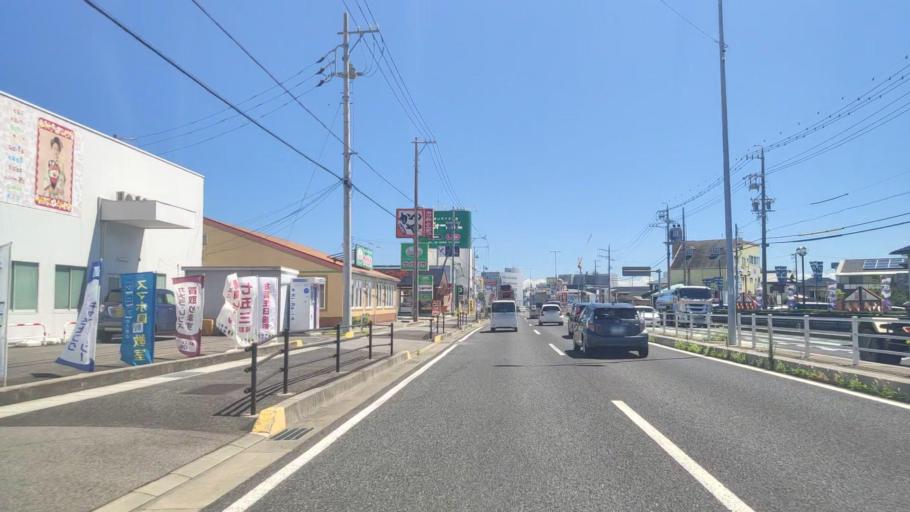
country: JP
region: Mie
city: Suzuka
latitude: 34.8407
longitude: 136.5885
